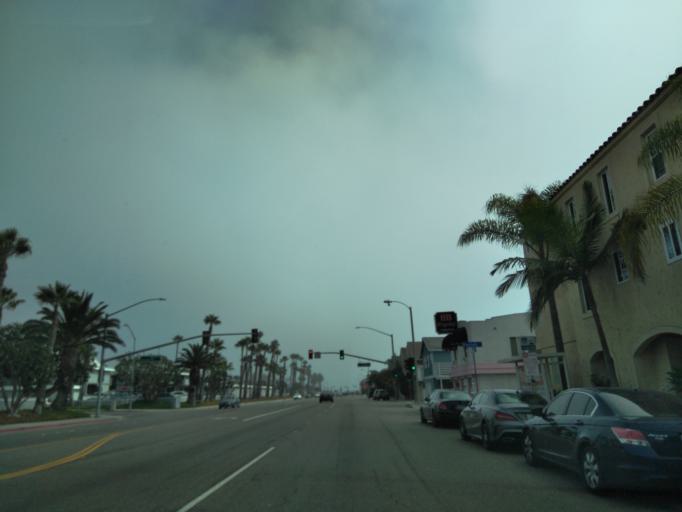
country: US
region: California
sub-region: Orange County
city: Seal Beach
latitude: 33.7146
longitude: -118.0666
